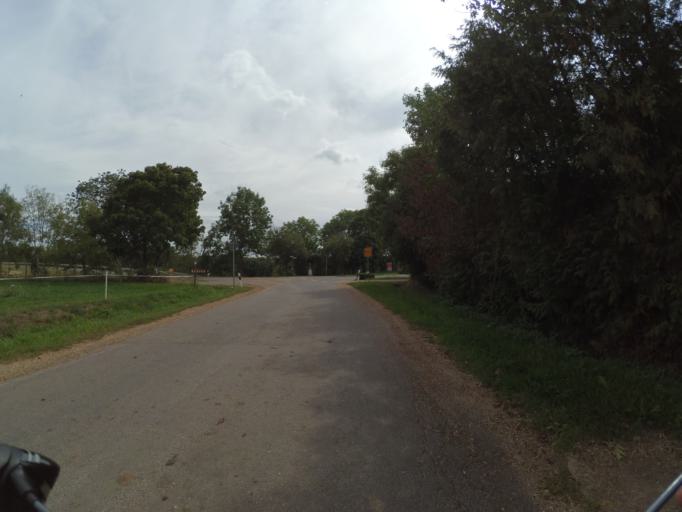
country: DE
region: Rheinland-Pfalz
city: Dodenburg
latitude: 49.9157
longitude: 6.7814
